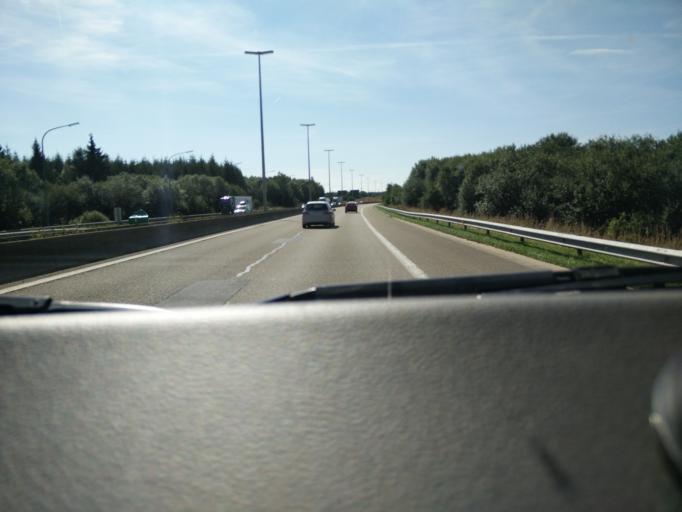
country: BE
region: Wallonia
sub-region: Province du Luxembourg
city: Leglise
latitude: 49.8579
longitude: 5.5093
